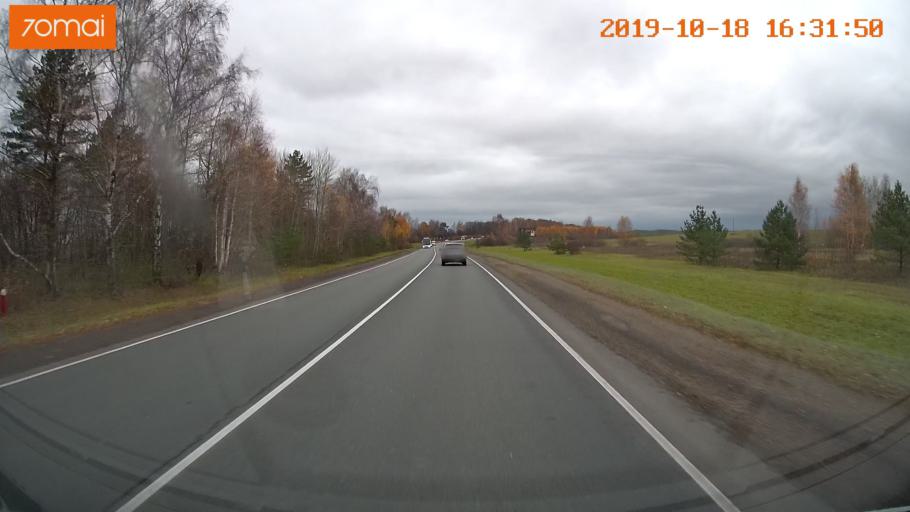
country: RU
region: Vladimir
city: Suzdal'
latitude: 56.3572
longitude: 40.4700
